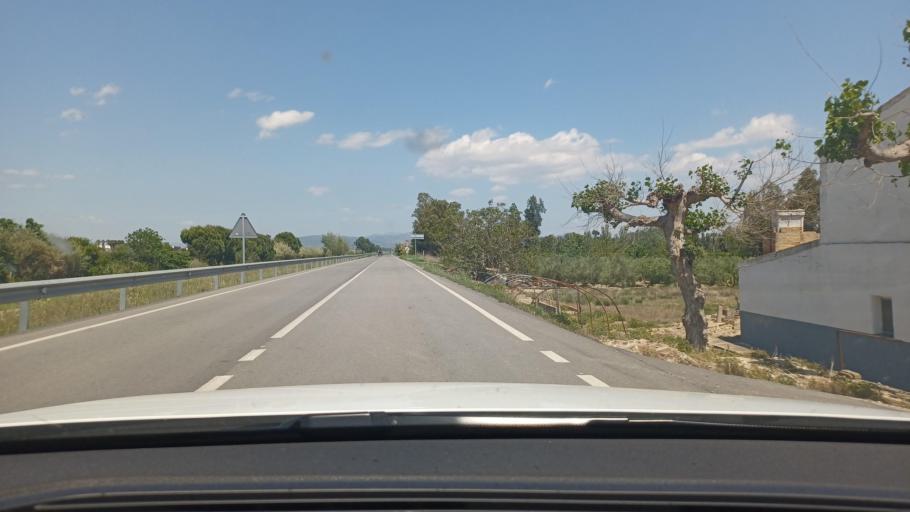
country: ES
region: Catalonia
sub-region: Provincia de Tarragona
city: Amposta
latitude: 40.6719
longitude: 0.5907
